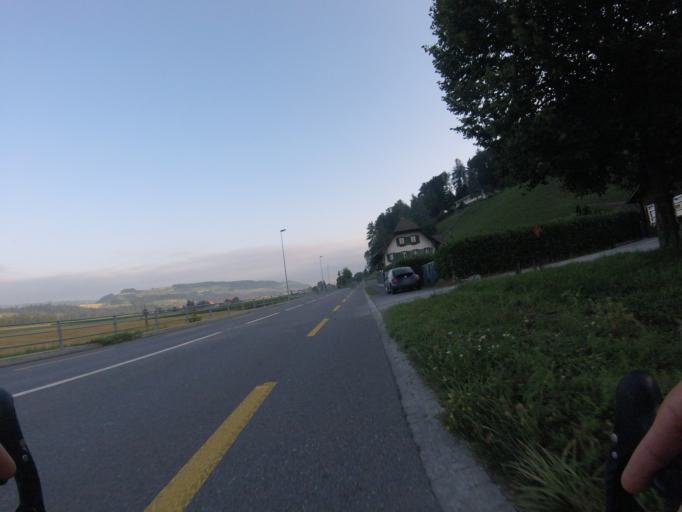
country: CH
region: Bern
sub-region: Bern-Mittelland District
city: Niederwichtrach
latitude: 46.8241
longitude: 7.5841
